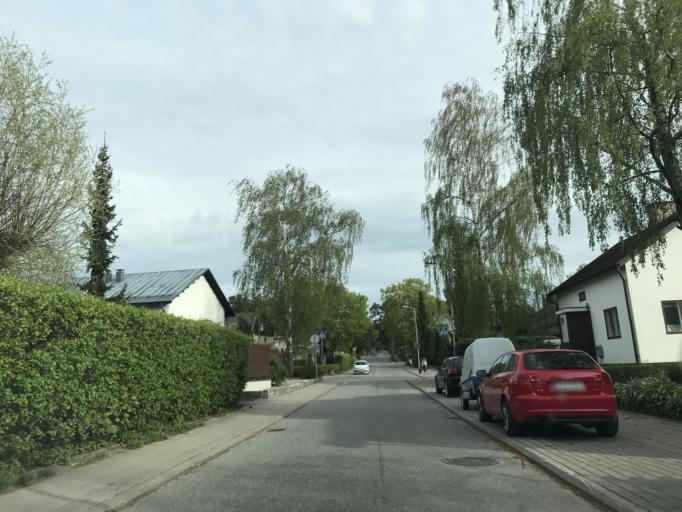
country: FI
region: Varsinais-Suomi
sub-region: Turku
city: Turku
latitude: 60.4388
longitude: 22.2990
